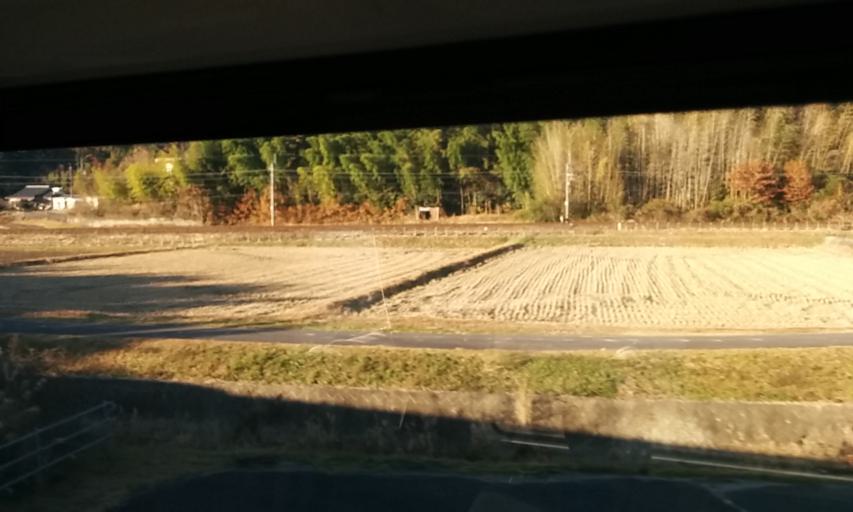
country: JP
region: Gifu
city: Nakatsugawa
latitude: 35.4773
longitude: 137.4798
